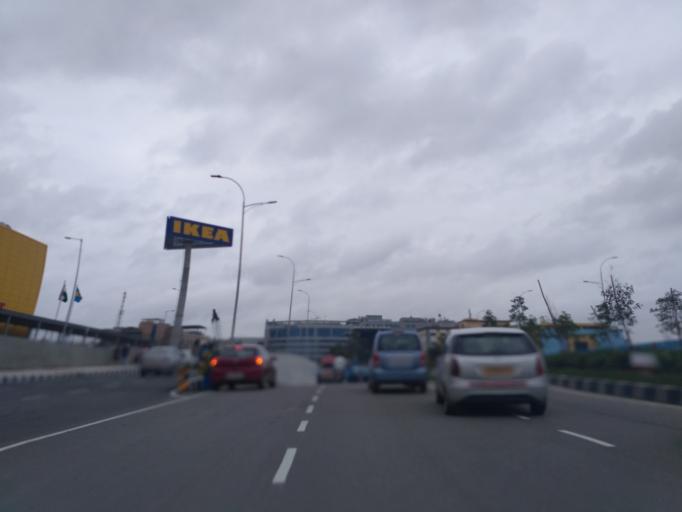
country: IN
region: Telangana
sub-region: Rangareddi
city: Kukatpalli
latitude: 17.4383
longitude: 78.3759
